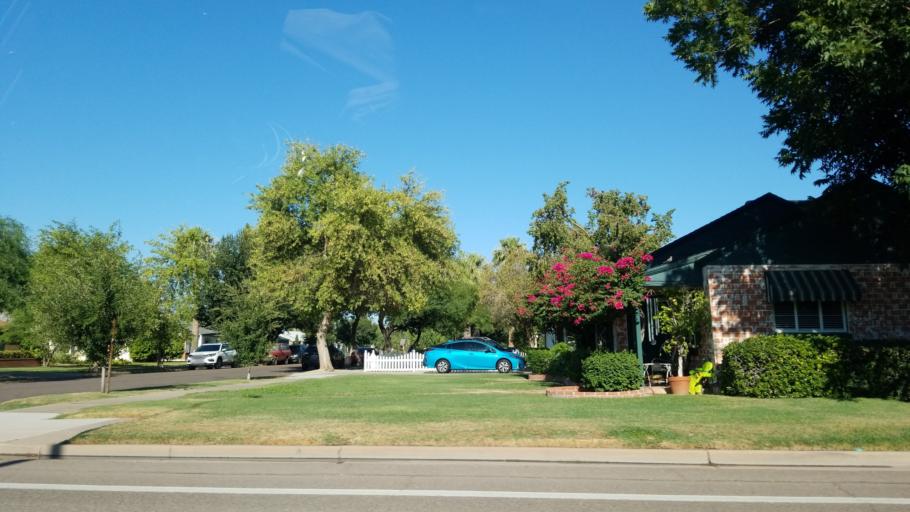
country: US
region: Arizona
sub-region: Maricopa County
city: Phoenix
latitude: 33.4759
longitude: -112.0804
